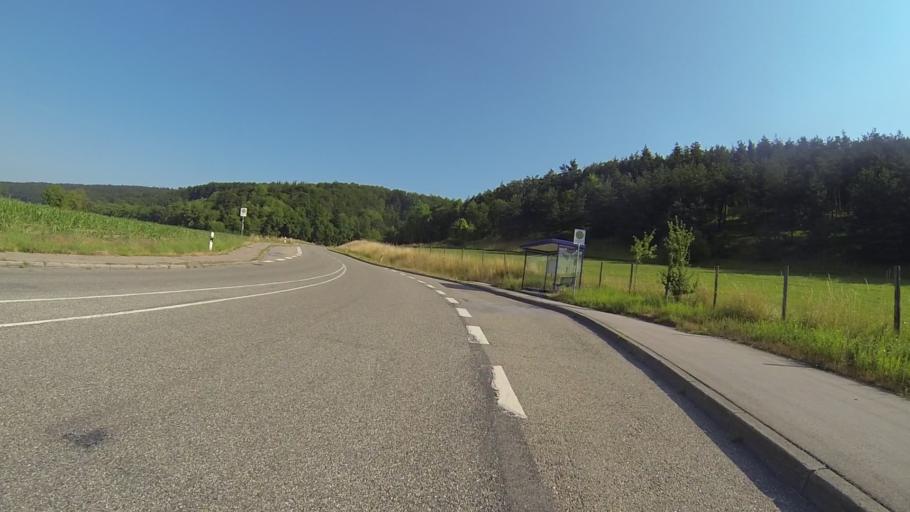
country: DE
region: Baden-Wuerttemberg
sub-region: Regierungsbezirk Stuttgart
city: Konigsbronn
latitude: 48.7339
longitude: 10.1381
